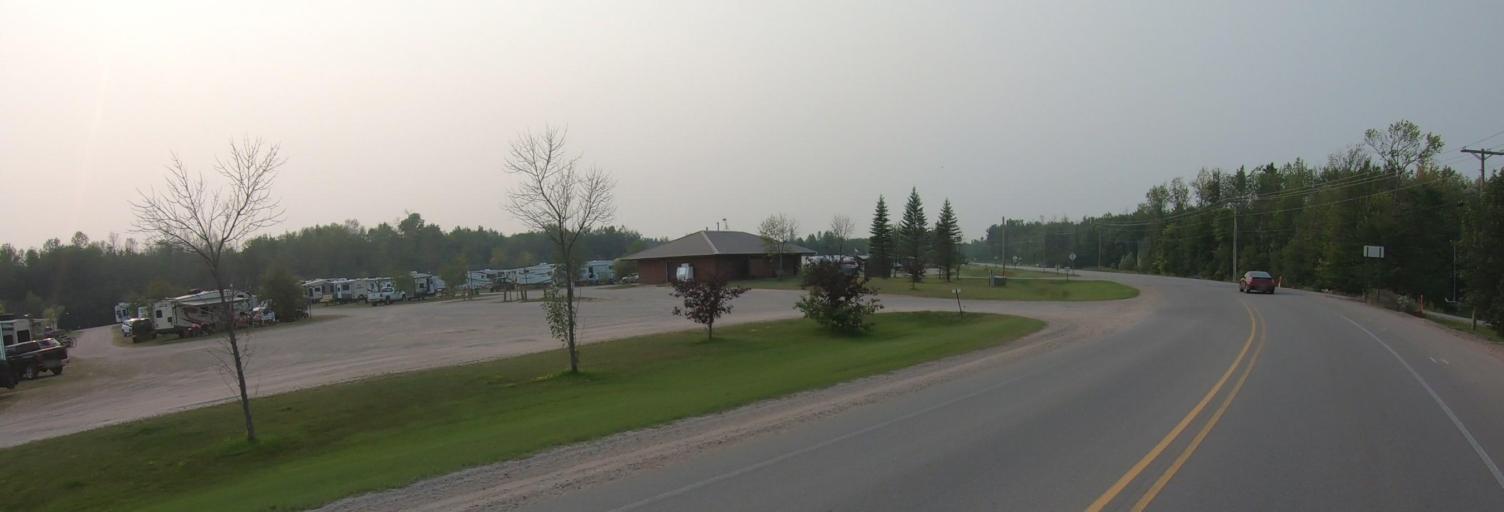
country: US
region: Michigan
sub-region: Chippewa County
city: Sault Ste. Marie
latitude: 46.4235
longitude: -84.6037
